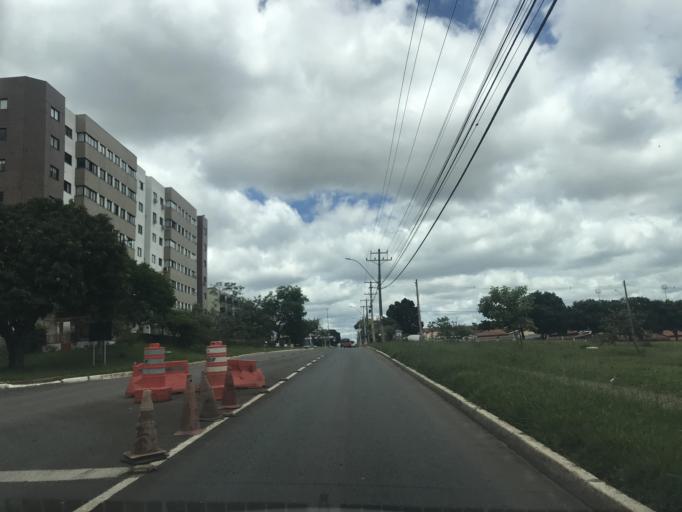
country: BR
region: Federal District
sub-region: Brasilia
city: Brasilia
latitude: -15.6531
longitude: -47.7912
